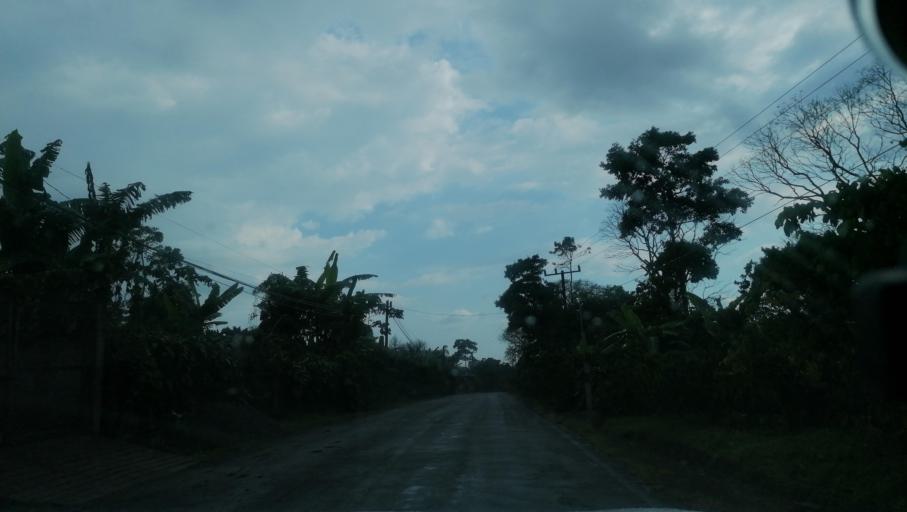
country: MX
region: Chiapas
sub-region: Cacahoatan
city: Benito Juarez
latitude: 15.0477
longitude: -92.1865
